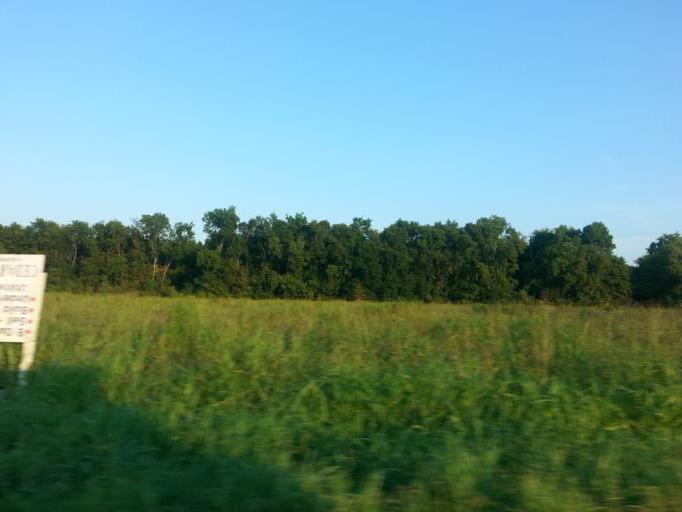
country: US
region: Tennessee
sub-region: Monroe County
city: Sweetwater
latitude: 35.5796
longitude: -84.4852
